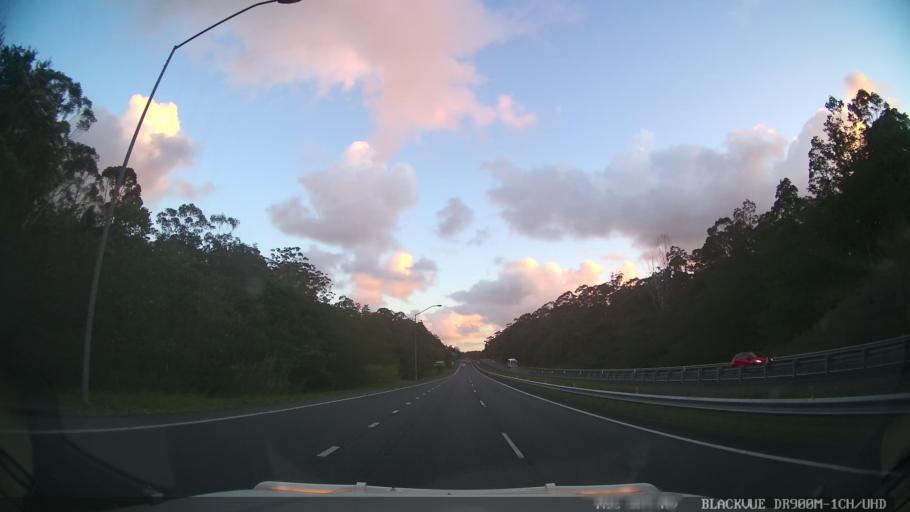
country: AU
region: Queensland
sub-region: Sunshine Coast
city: Twin Waters
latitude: -26.5947
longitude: 152.9712
